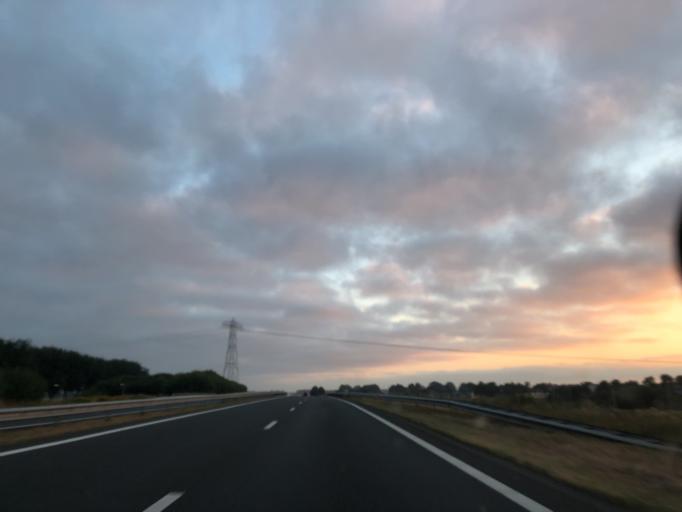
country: NL
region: Groningen
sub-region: Gemeente Veendam
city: Veendam
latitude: 53.1334
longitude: 6.8996
